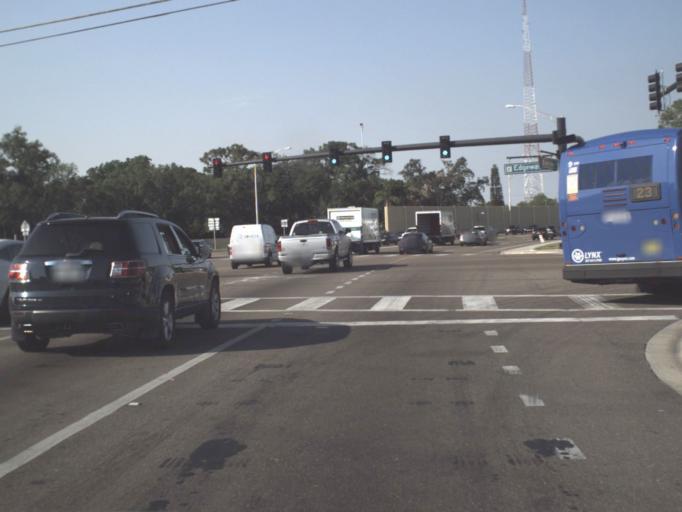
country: US
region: Florida
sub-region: Orange County
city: Fairview Shores
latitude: 28.6107
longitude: -81.4151
